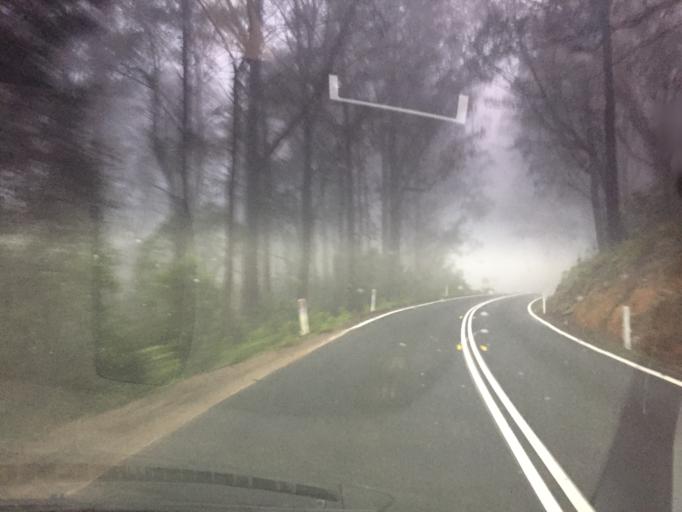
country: AU
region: New South Wales
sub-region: Bombala
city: Bombala
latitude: -36.5988
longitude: 149.4426
